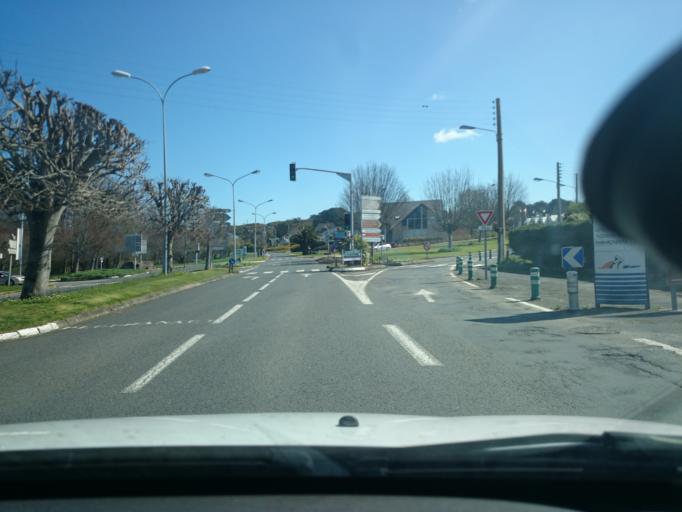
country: FR
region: Brittany
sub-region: Departement des Cotes-d'Armor
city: Tregastel
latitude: 48.8238
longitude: -3.4806
